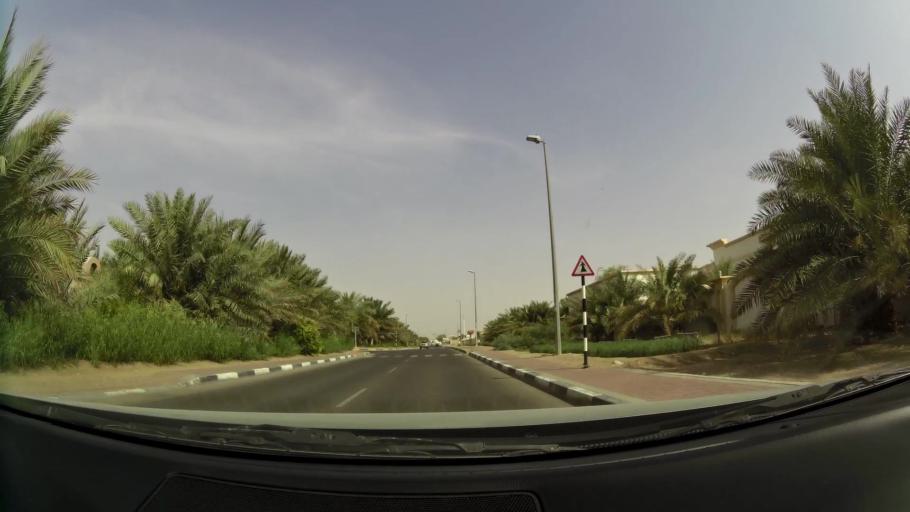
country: AE
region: Abu Dhabi
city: Al Ain
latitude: 24.1545
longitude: 55.6902
